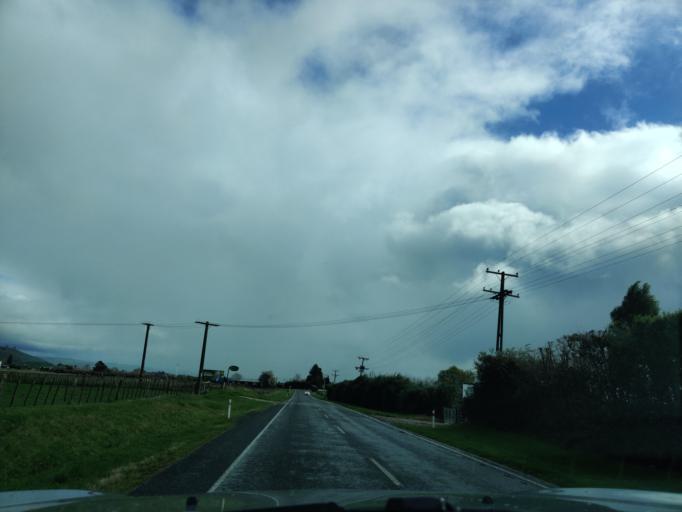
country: NZ
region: Hawke's Bay
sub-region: Hastings District
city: Hastings
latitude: -39.6781
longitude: 176.8303
